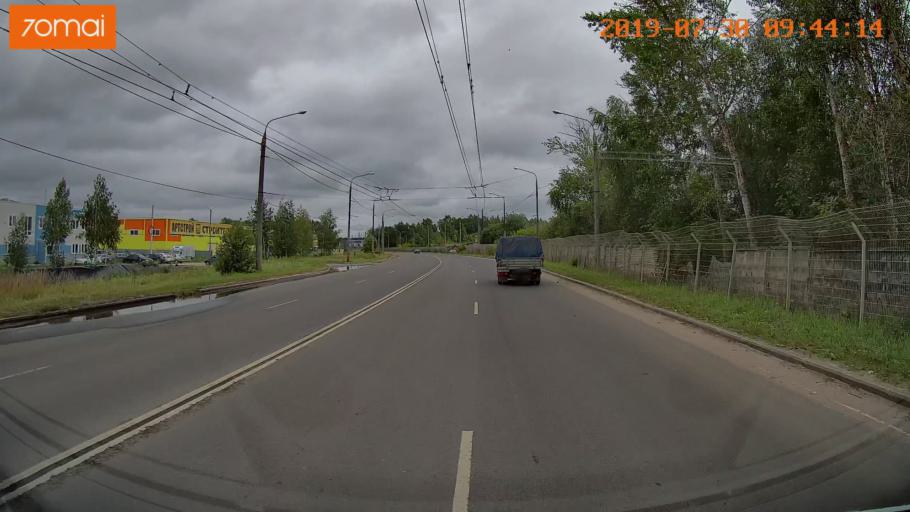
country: RU
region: Ivanovo
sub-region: Gorod Ivanovo
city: Ivanovo
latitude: 56.9490
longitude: 40.9606
